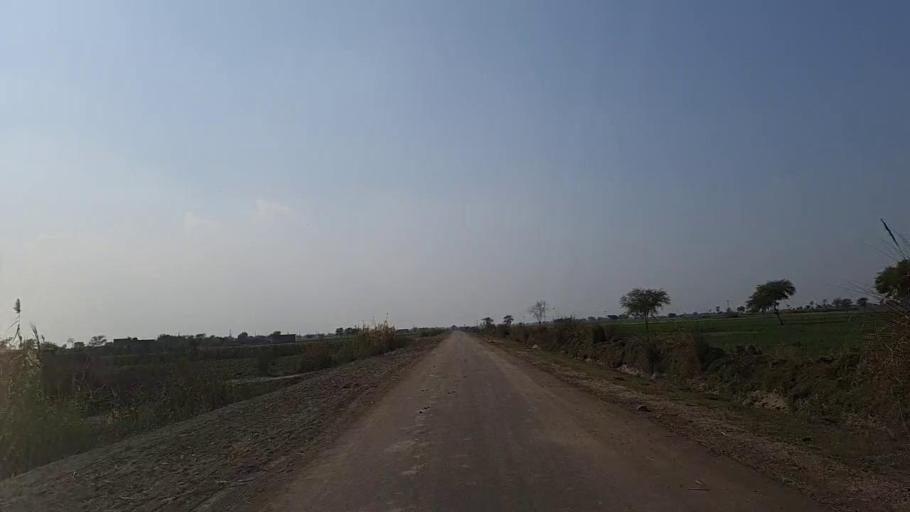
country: PK
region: Sindh
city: Jam Sahib
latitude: 26.3001
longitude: 68.5793
